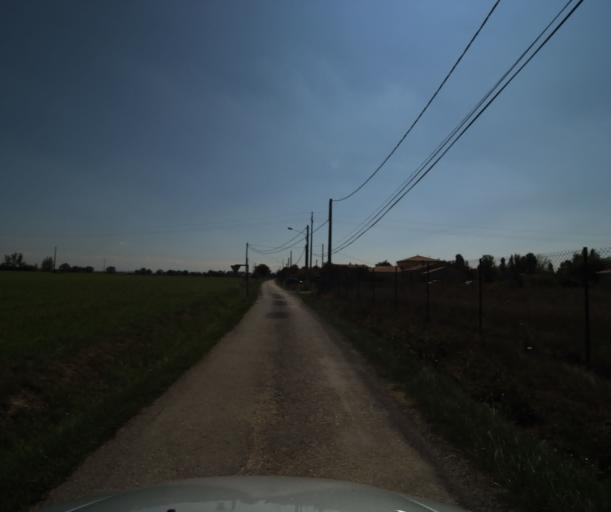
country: FR
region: Midi-Pyrenees
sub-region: Departement de la Haute-Garonne
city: Labastidette
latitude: 43.4412
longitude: 1.2638
